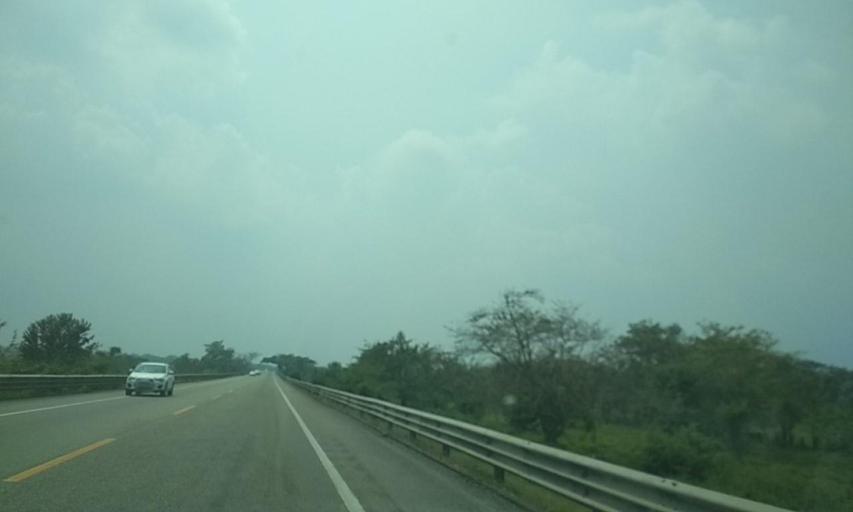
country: MX
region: Tabasco
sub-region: Huimanguillo
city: Francisco Rueda
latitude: 17.7674
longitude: -94.0301
